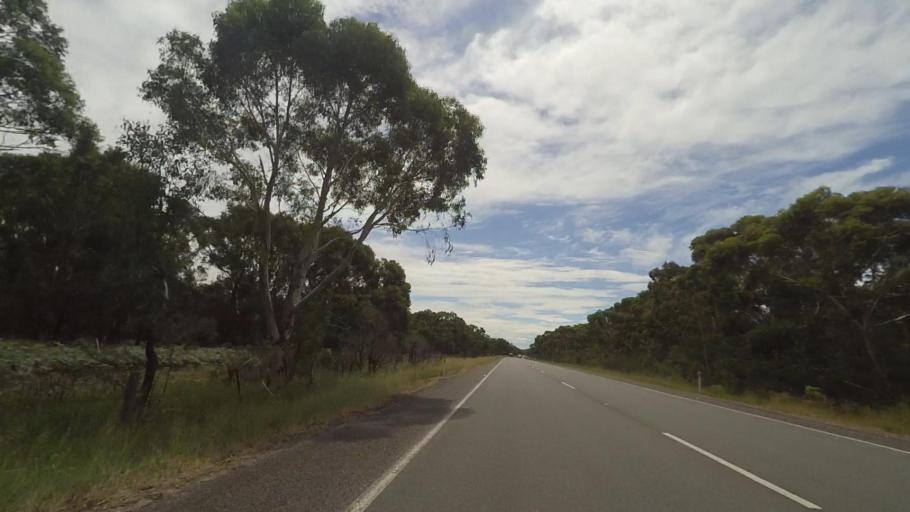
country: AU
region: New South Wales
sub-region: Port Stephens Shire
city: Medowie
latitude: -32.7842
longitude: 151.8932
